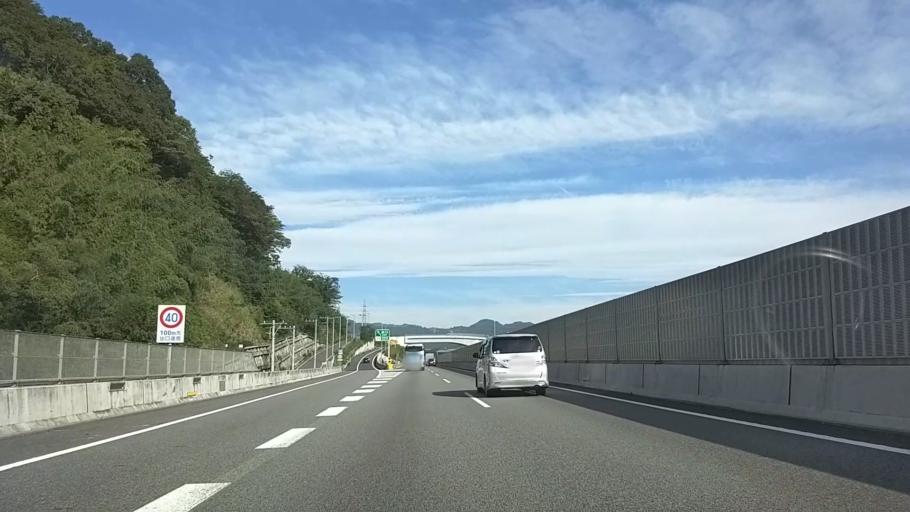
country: JP
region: Tokyo
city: Hachioji
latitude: 35.5782
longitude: 139.2963
